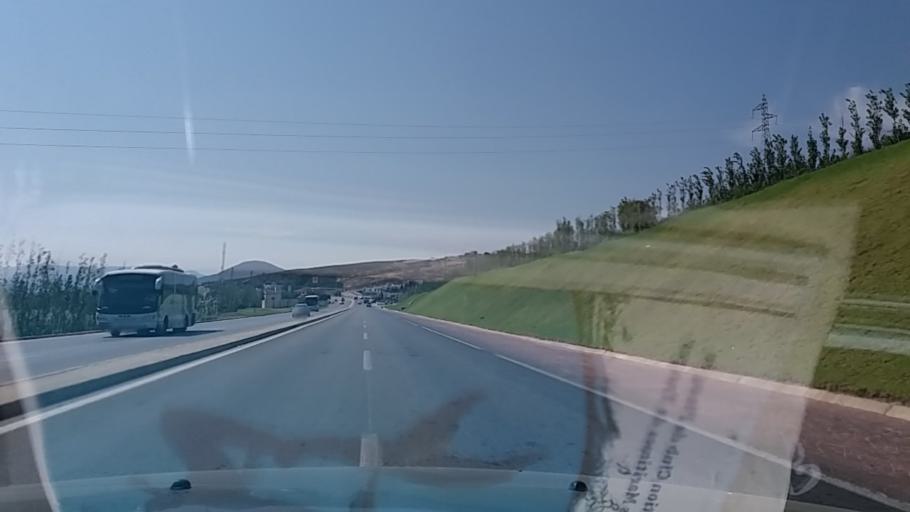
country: MA
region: Tanger-Tetouan
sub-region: Tetouan
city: Saddina
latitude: 35.5601
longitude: -5.4405
